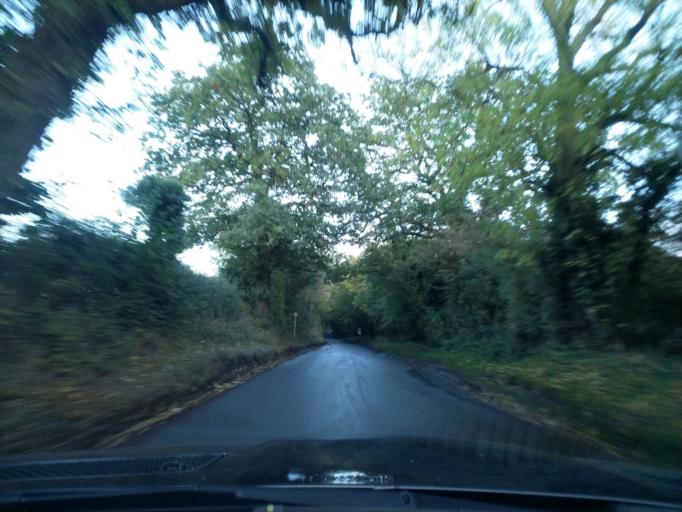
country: GB
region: England
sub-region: Solihull
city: Knowle
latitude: 52.3482
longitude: -1.7126
